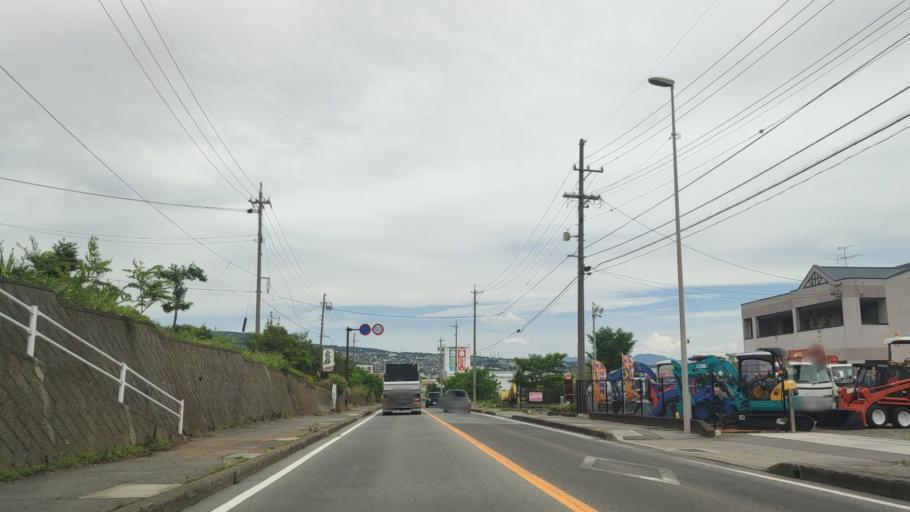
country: JP
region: Nagano
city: Komoro
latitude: 36.3388
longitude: 138.3992
